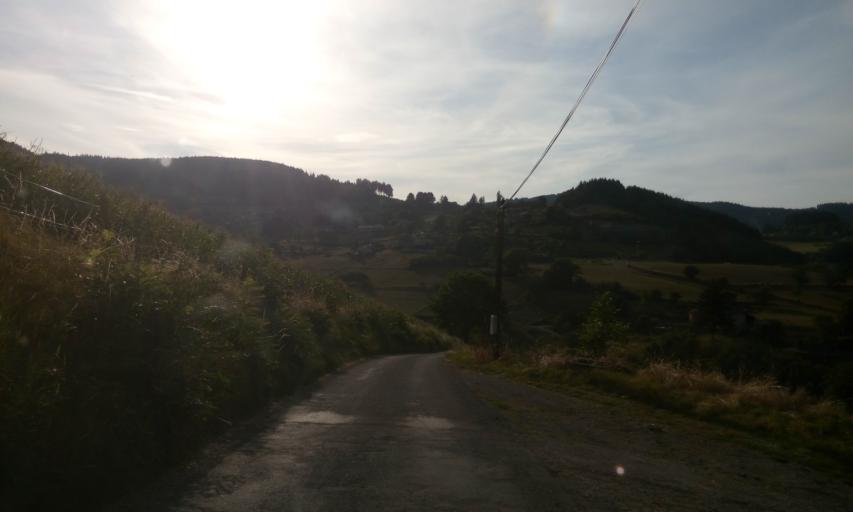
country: FR
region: Rhone-Alpes
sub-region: Departement du Rhone
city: Grandris
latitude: 45.9962
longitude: 4.4521
